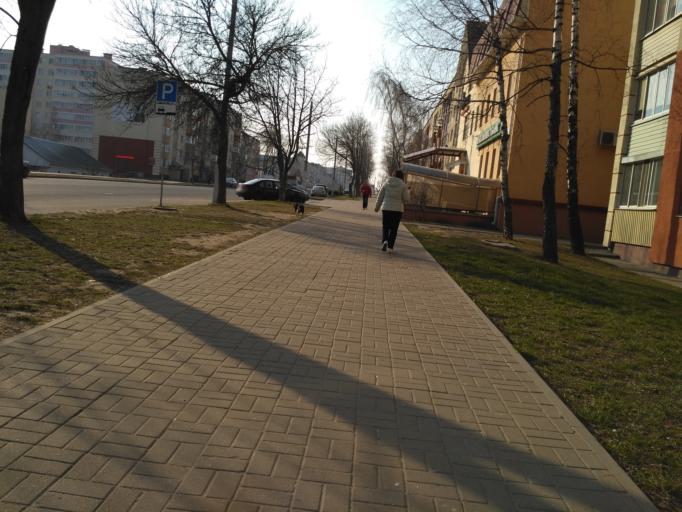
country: BY
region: Minsk
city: Zaslawye
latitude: 54.0113
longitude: 27.2691
